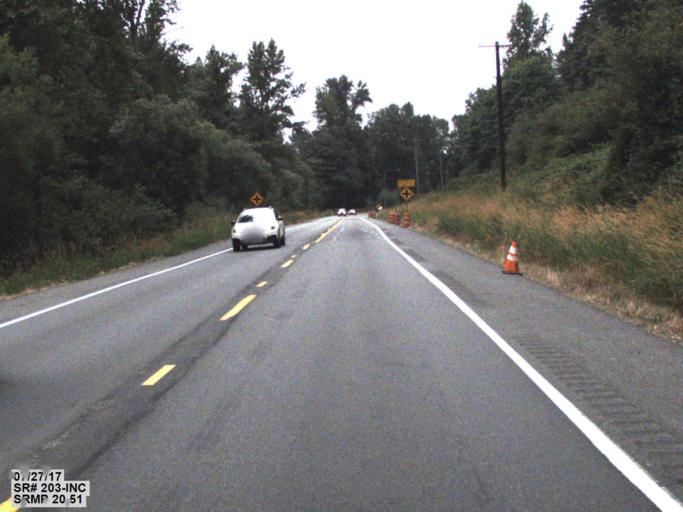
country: US
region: Washington
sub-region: Snohomish County
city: Monroe
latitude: 47.8089
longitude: -121.9818
